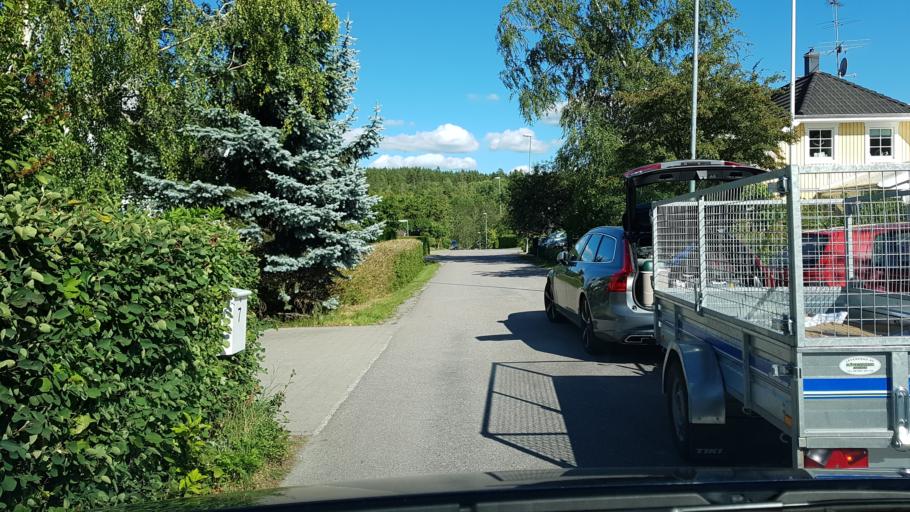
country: SE
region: Stockholm
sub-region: Upplands-Bro Kommun
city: Kungsaengen
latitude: 59.4779
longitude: 17.8013
